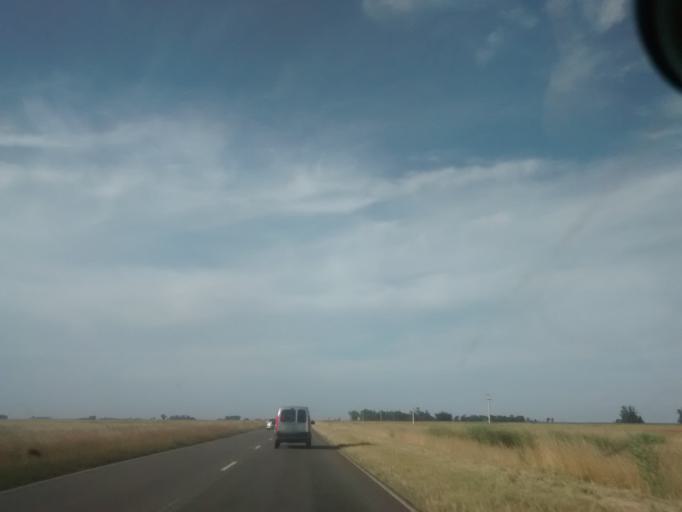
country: AR
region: Buenos Aires
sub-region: Partido de Ayacucho
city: Ayacucho
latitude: -37.0750
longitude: -58.5449
